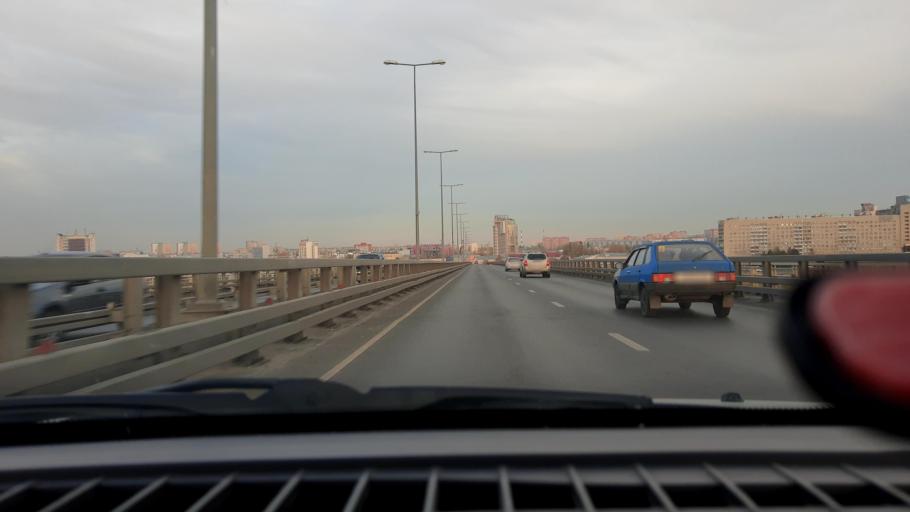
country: RU
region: Nizjnij Novgorod
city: Nizhniy Novgorod
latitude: 56.3202
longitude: 43.9637
